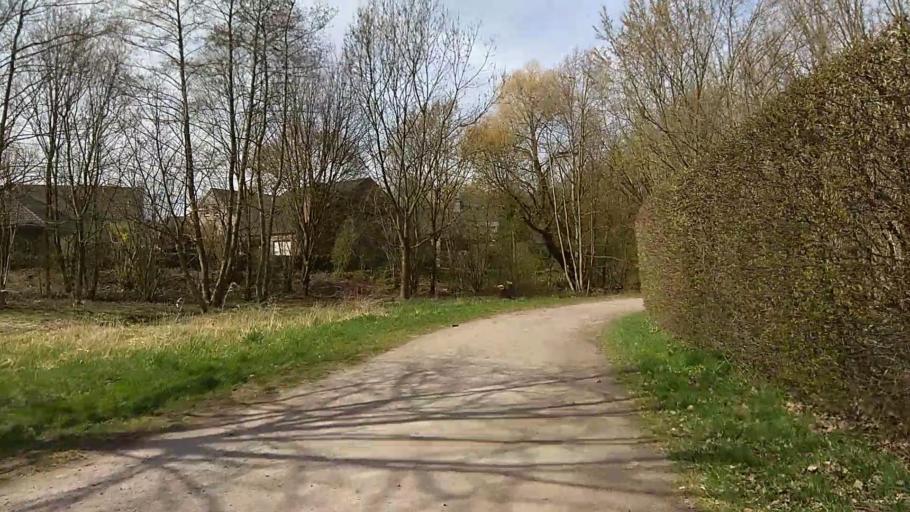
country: DE
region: North Rhine-Westphalia
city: Herten
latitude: 51.5680
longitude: 7.0960
